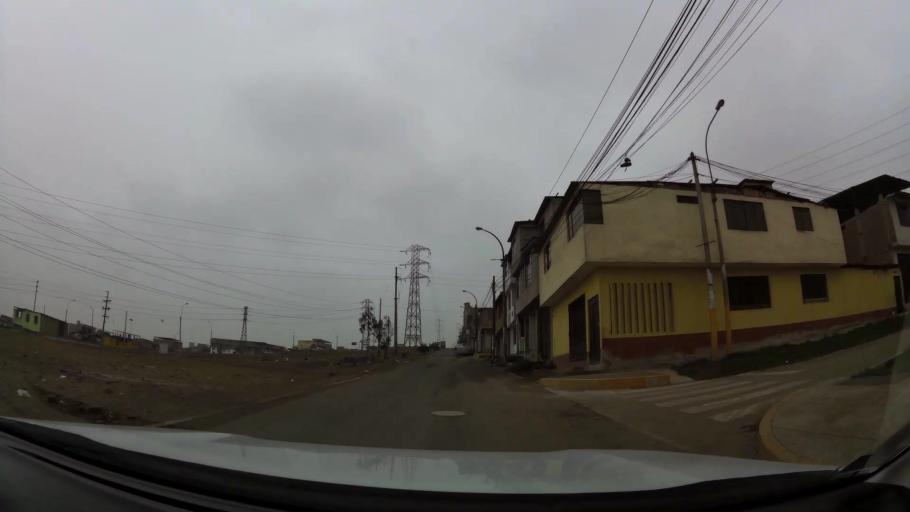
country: PE
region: Lima
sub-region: Lima
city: Surco
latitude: -12.2163
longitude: -76.9205
